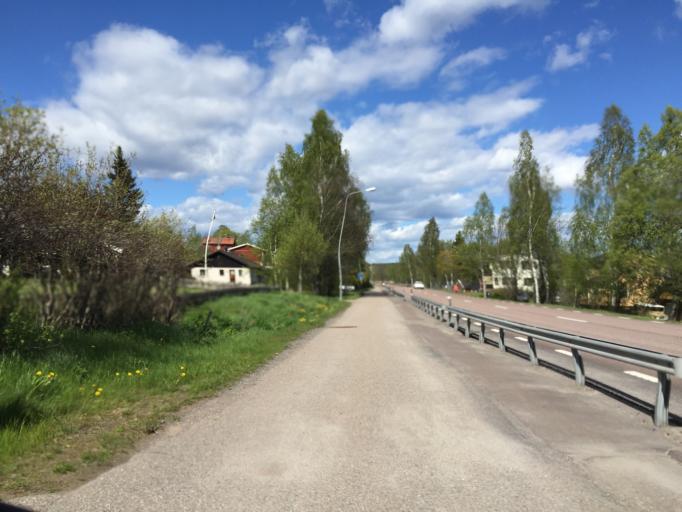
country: SE
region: Dalarna
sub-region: Ludvika Kommun
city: Ludvika
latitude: 60.1777
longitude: 15.2055
